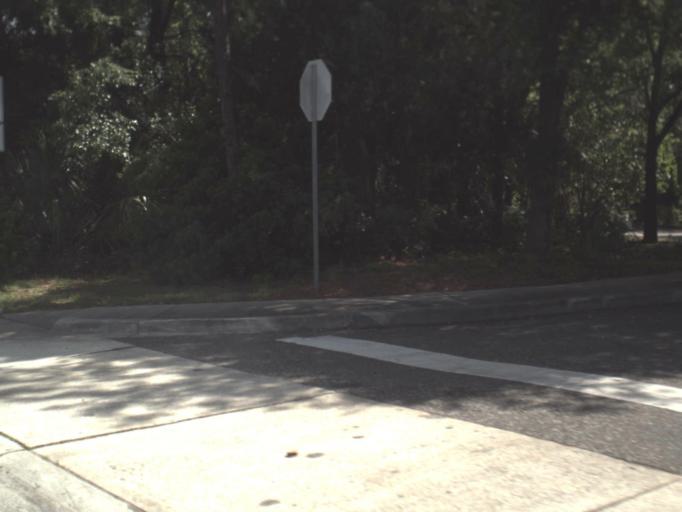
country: US
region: Florida
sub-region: Duval County
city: Jacksonville
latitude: 30.2989
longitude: -81.6014
